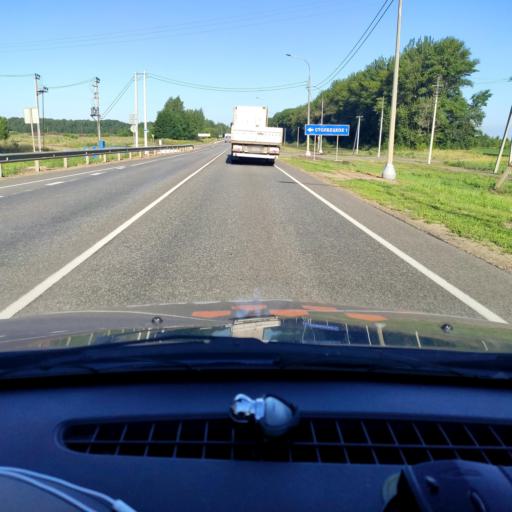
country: RU
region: Orjol
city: Zmiyevka
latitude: 52.6352
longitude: 36.6140
